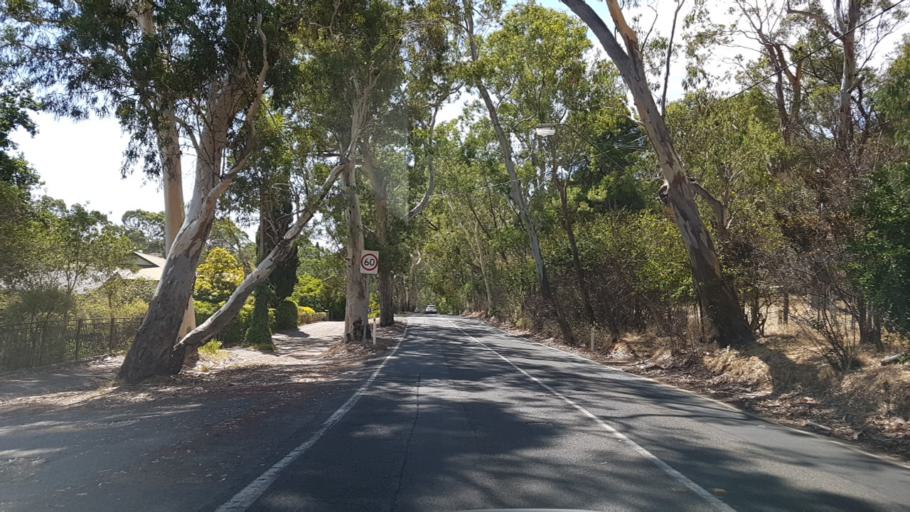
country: AU
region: South Australia
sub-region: Mitcham
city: Belair
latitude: -35.0057
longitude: 138.6330
